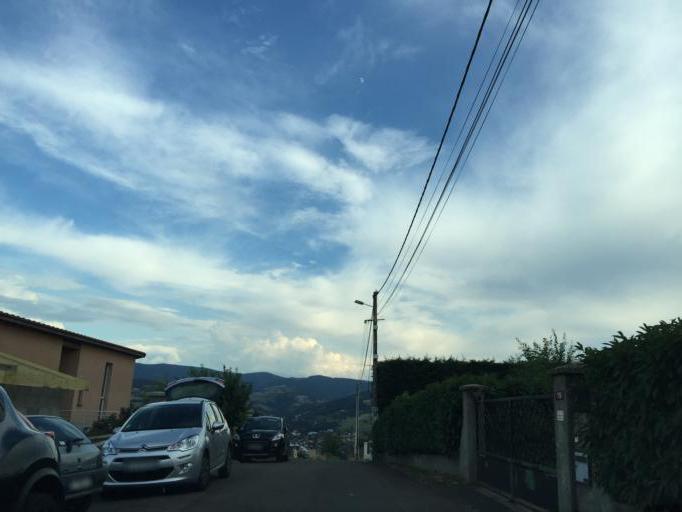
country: FR
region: Rhone-Alpes
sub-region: Departement de la Loire
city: Saint-Chamond
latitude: 45.4831
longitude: 4.4906
